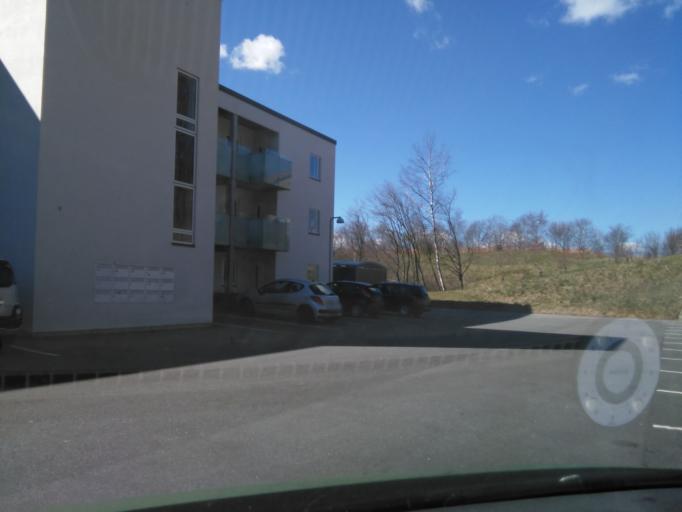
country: DK
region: Central Jutland
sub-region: Arhus Kommune
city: Arhus
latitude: 56.1095
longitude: 10.2103
